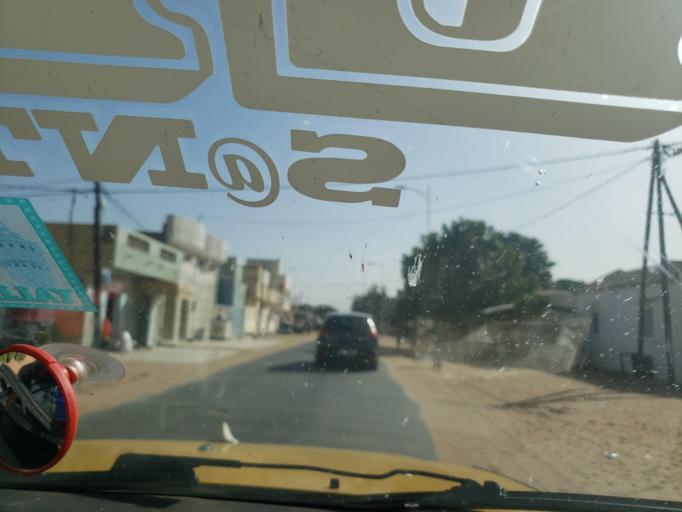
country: SN
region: Louga
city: Louga
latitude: 15.6255
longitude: -16.2137
